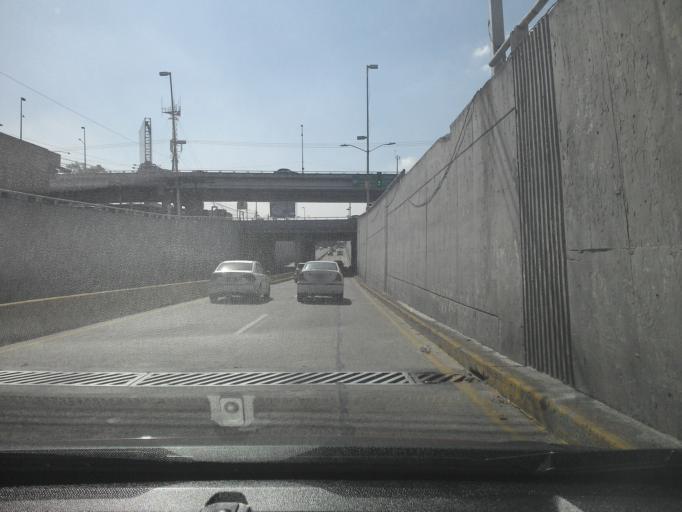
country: MX
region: Jalisco
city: Guadalajara
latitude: 20.6800
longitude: -103.4212
